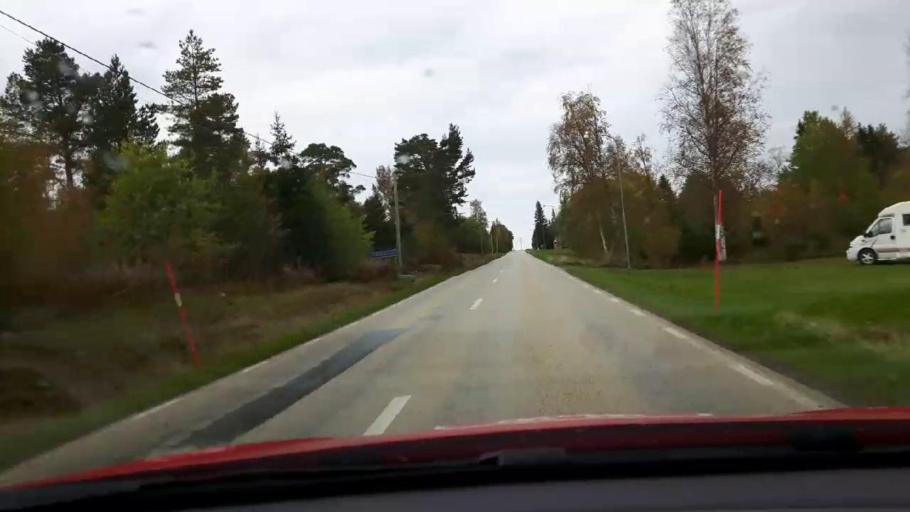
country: SE
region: Jaemtland
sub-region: Bergs Kommun
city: Hoverberg
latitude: 62.9834
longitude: 14.3425
